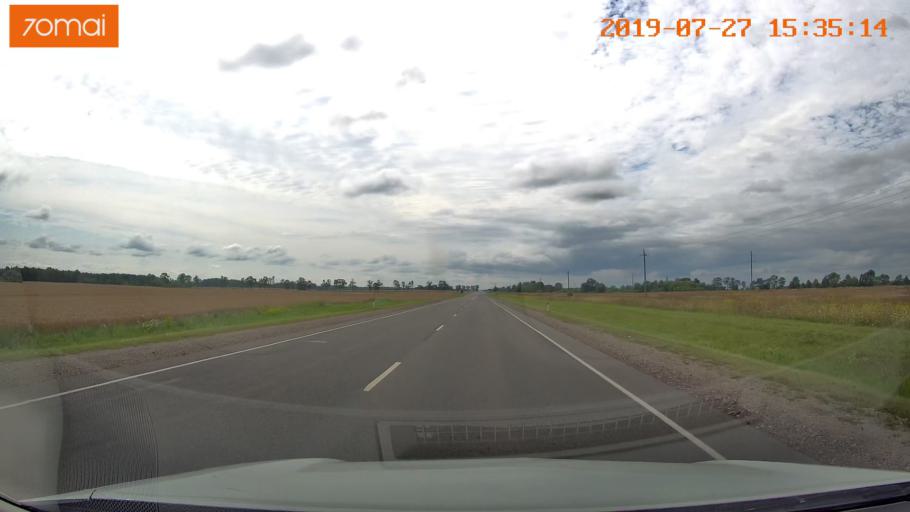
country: RU
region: Kaliningrad
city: Nesterov
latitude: 54.6139
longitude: 22.4025
